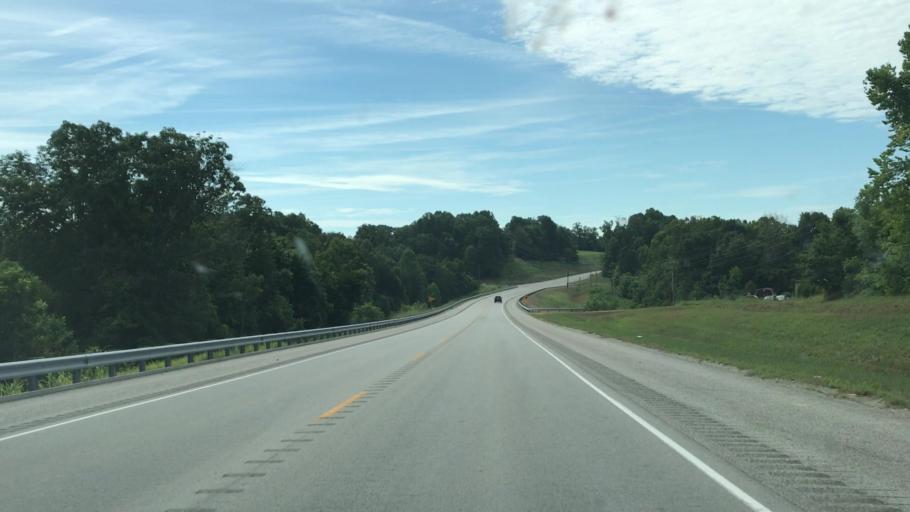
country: US
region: Kentucky
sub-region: Edmonson County
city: Brownsville
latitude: 37.1636
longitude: -86.2252
